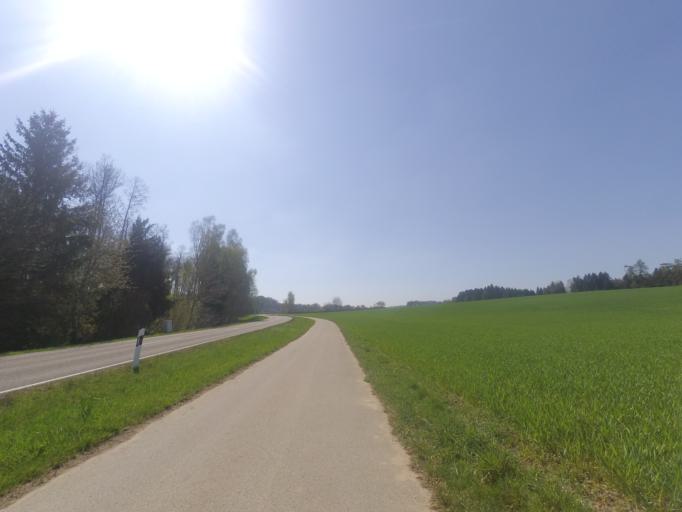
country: DE
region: Bavaria
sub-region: Swabia
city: Roggenburg
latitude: 48.3219
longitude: 10.2116
